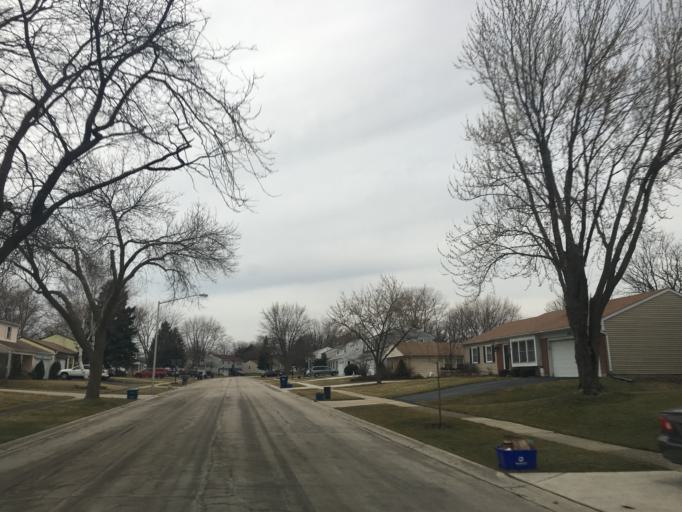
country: US
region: Illinois
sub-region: Cook County
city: Schaumburg
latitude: 42.0266
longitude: -88.1153
